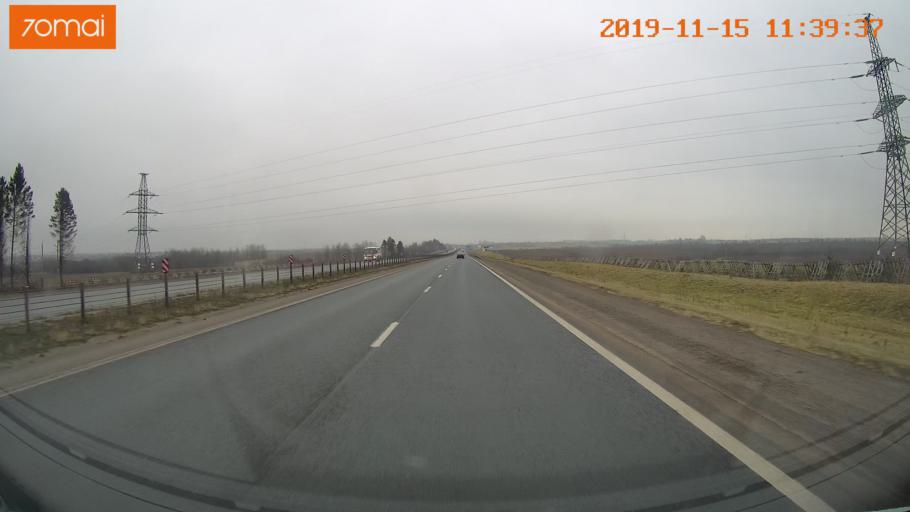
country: RU
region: Vologda
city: Molochnoye
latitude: 59.2117
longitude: 39.7295
